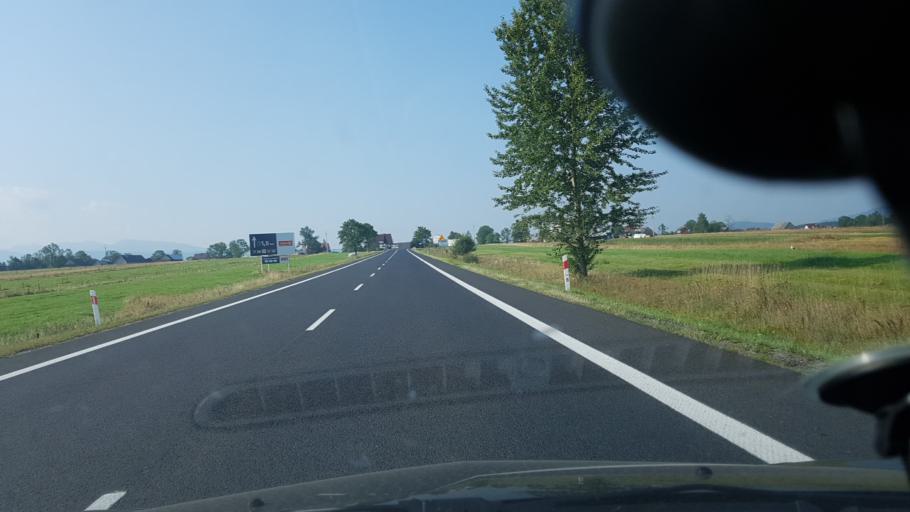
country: PL
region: Lesser Poland Voivodeship
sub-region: Powiat nowotarski
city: Chyzne
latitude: 49.4309
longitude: 19.6770
